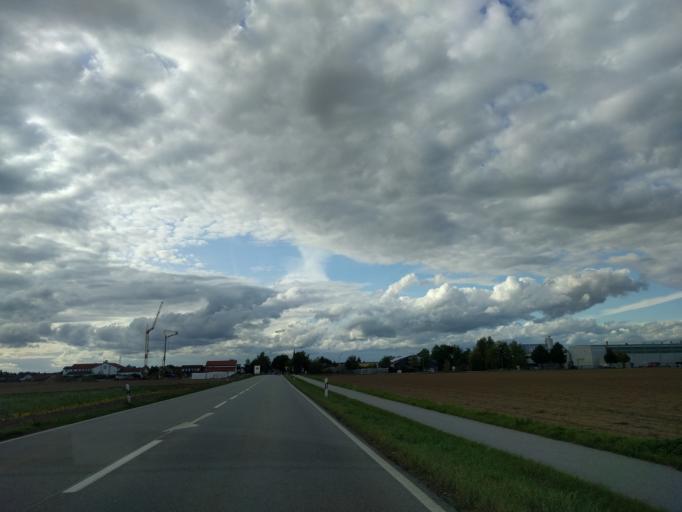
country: DE
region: Bavaria
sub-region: Lower Bavaria
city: Strasskirchen
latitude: 48.8263
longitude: 12.7334
